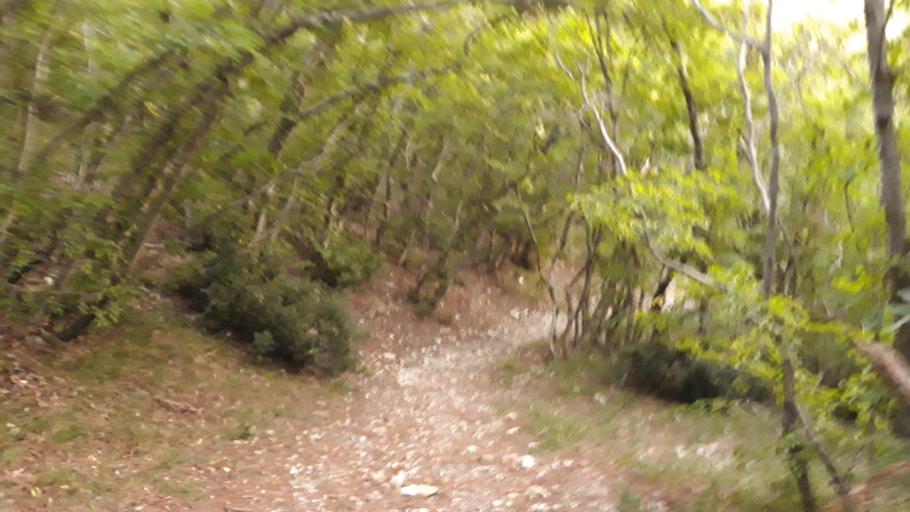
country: RU
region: Krasnodarskiy
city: Gelendzhik
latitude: 44.5822
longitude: 38.0863
